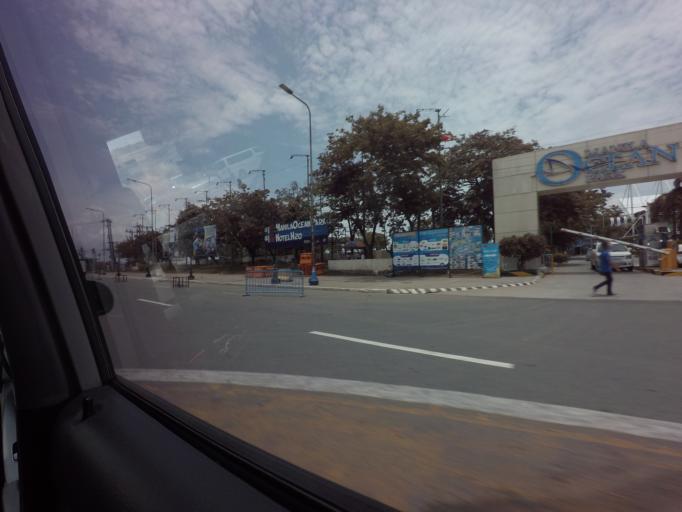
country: PH
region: Metro Manila
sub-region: City of Manila
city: Port Area
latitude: 14.5794
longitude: 120.9747
